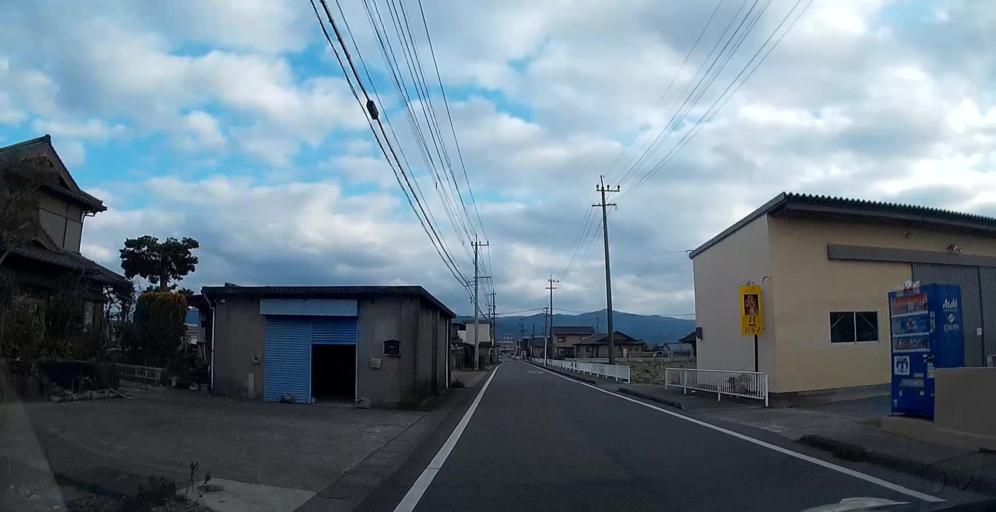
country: JP
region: Kumamoto
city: Yatsushiro
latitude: 32.5428
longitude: 130.6222
